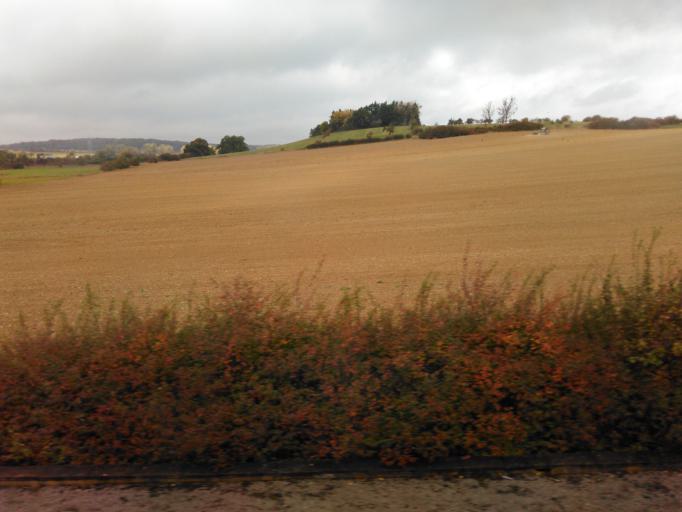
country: LU
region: Luxembourg
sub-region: Canton d'Esch-sur-Alzette
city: Bettembourg
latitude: 49.5322
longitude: 6.1218
